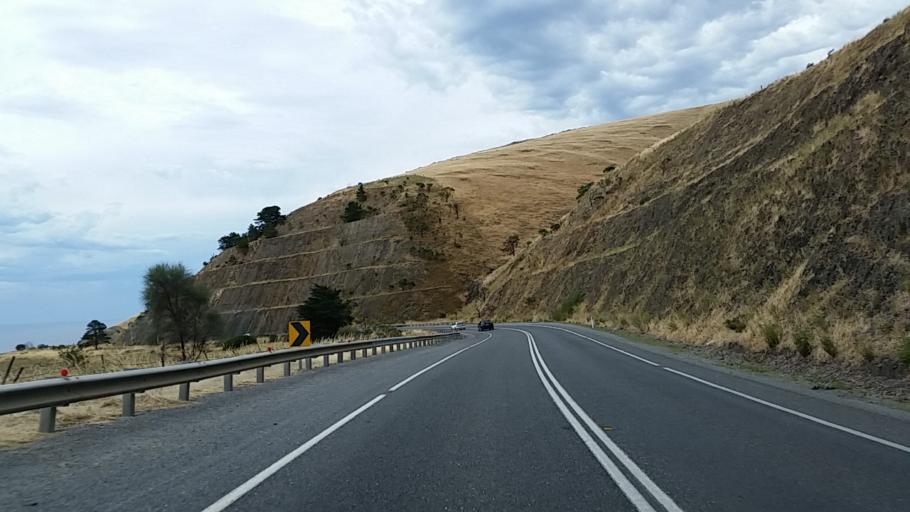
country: AU
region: South Australia
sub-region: Onkaparinga
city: Aldinga
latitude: -35.3654
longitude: 138.4562
